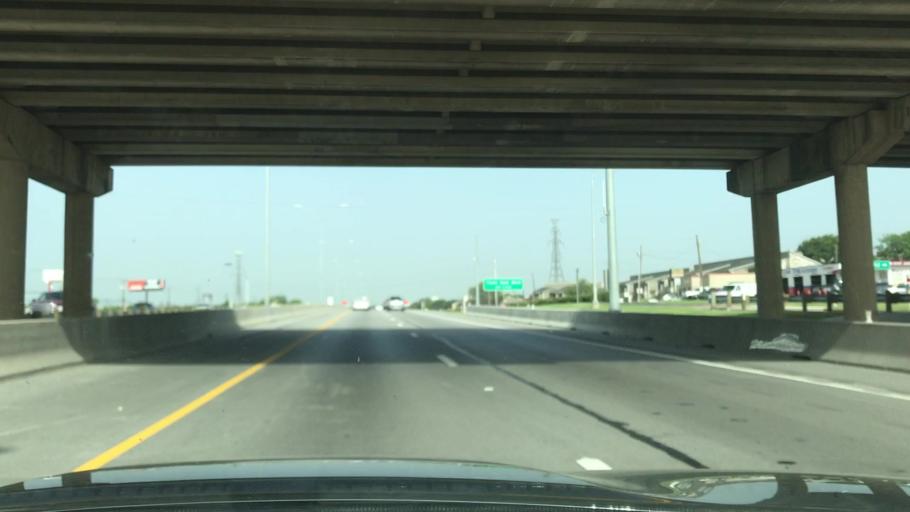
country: US
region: Texas
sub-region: Dallas County
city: Mesquite
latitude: 32.7925
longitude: -96.6338
